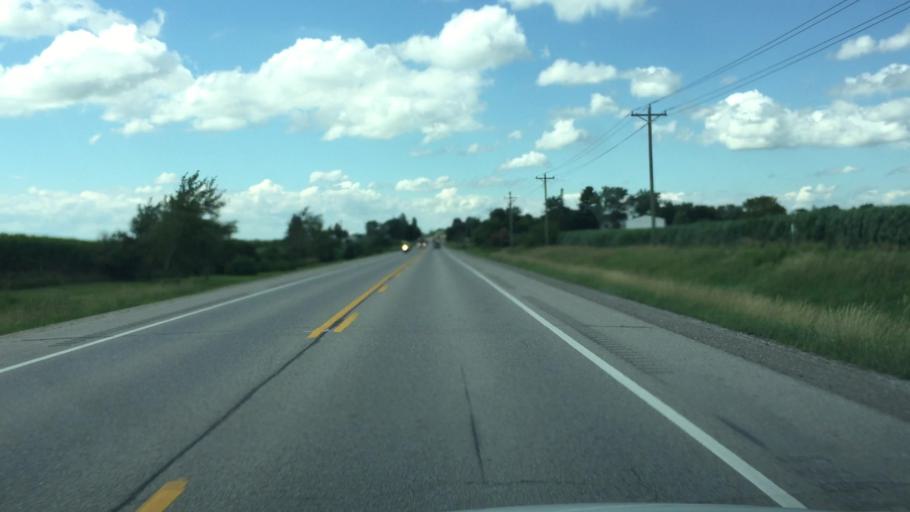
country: US
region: Iowa
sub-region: Johnson County
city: Solon
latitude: 41.7862
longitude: -91.4866
